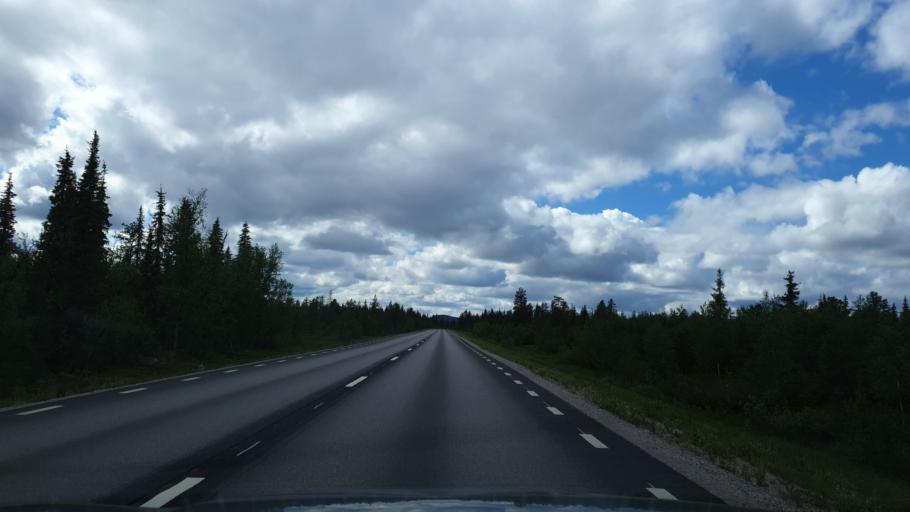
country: SE
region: Norrbotten
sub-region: Gallivare Kommun
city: Gaellivare
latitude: 67.0638
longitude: 20.2441
